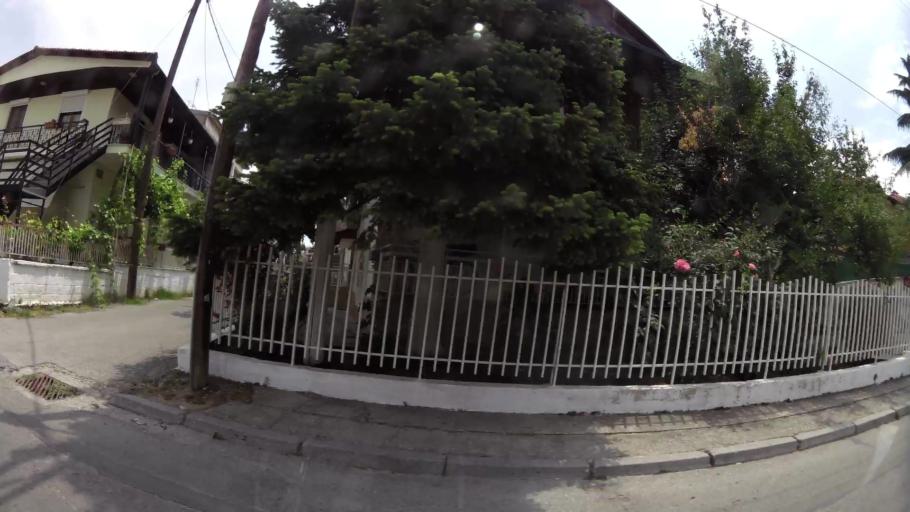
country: GR
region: Central Macedonia
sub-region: Nomos Pierias
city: Katerini
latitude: 40.2652
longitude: 22.5147
